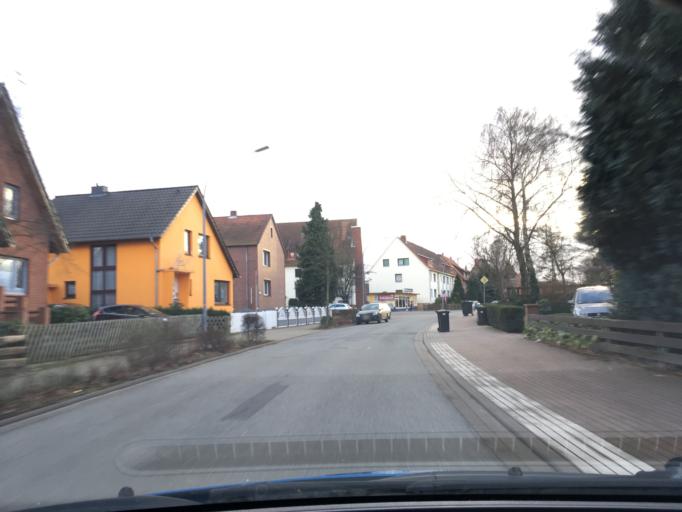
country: DE
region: Lower Saxony
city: Winsen
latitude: 53.3617
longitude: 10.2153
